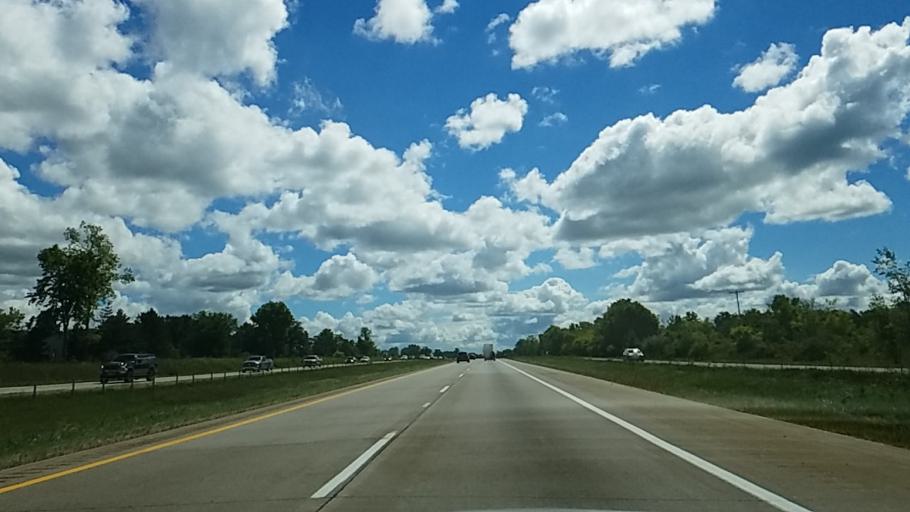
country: US
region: Michigan
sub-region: Genesee County
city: Fenton
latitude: 42.6879
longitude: -83.7607
